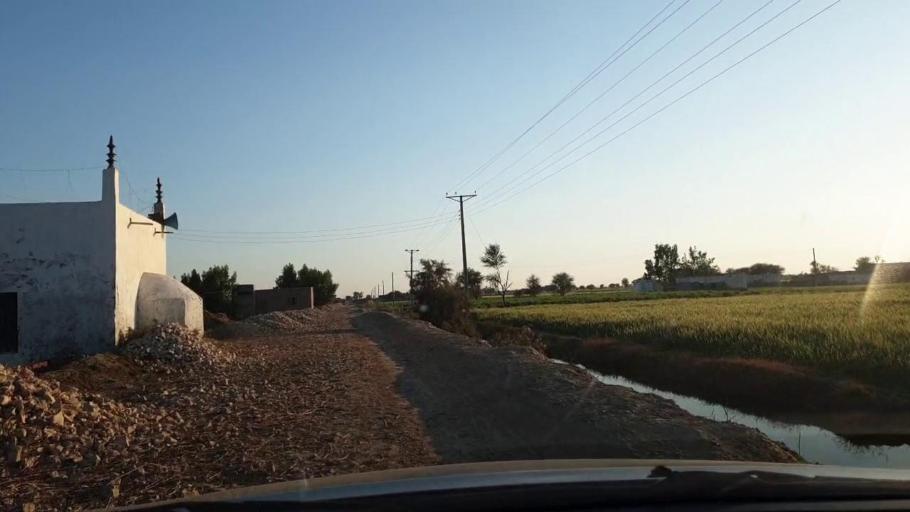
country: PK
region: Sindh
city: Tando Mittha Khan
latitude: 25.8372
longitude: 69.1615
